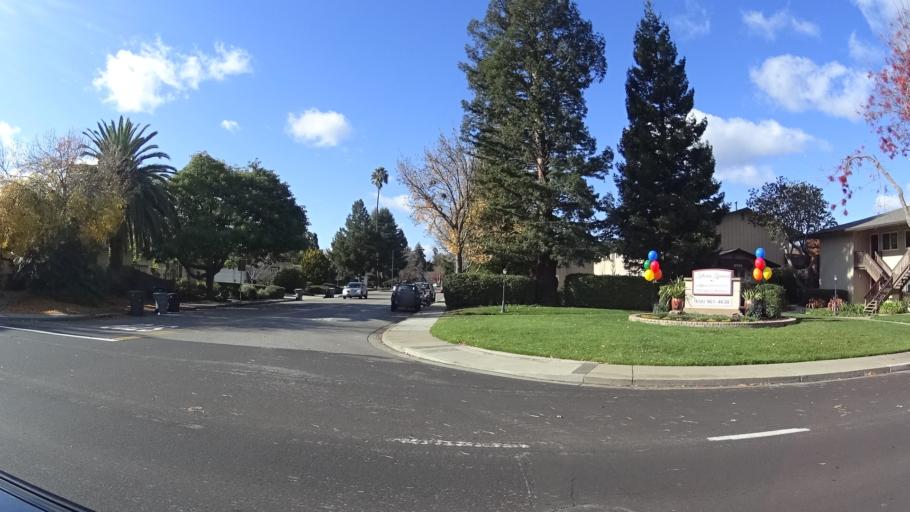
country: US
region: California
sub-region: Santa Clara County
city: Mountain View
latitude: 37.3785
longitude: -122.0628
